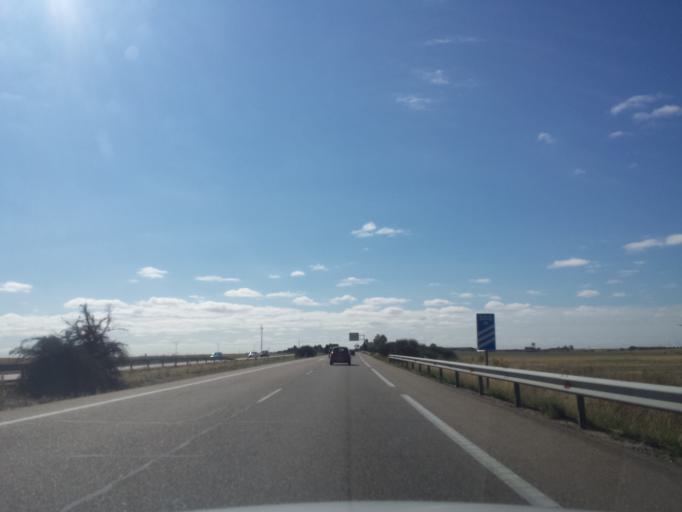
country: ES
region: Castille and Leon
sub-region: Provincia de Zamora
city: San Esteban del Molar
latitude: 41.9479
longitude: -5.5625
